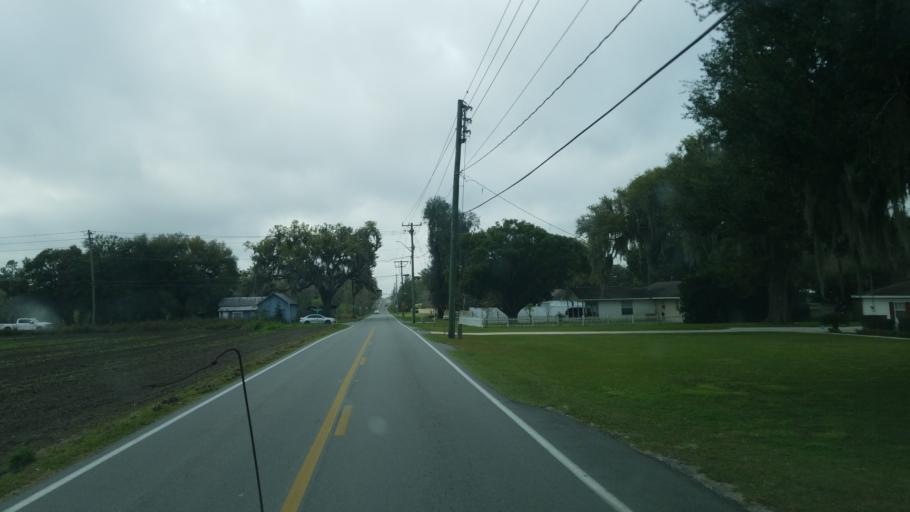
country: US
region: Florida
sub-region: Polk County
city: Kathleen
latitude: 28.1437
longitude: -82.0234
